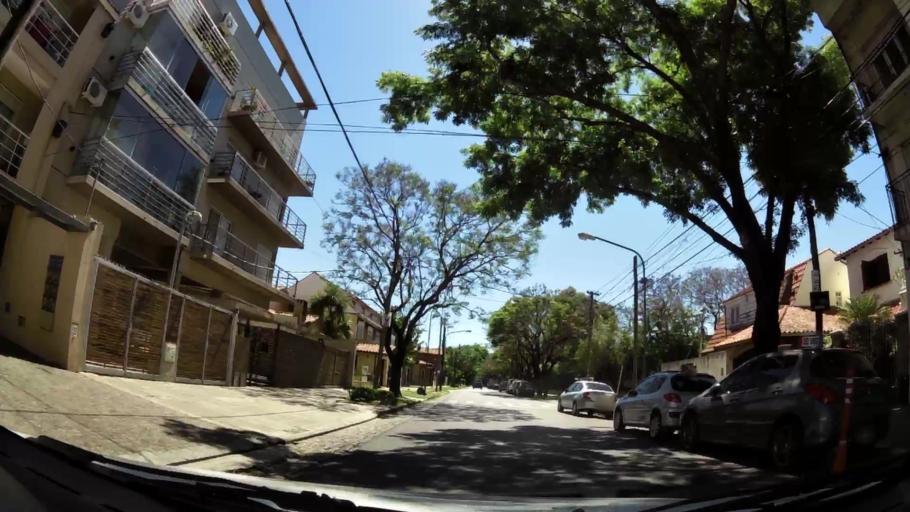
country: AR
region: Buenos Aires
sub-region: Partido de Vicente Lopez
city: Olivos
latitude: -34.5214
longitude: -58.5064
